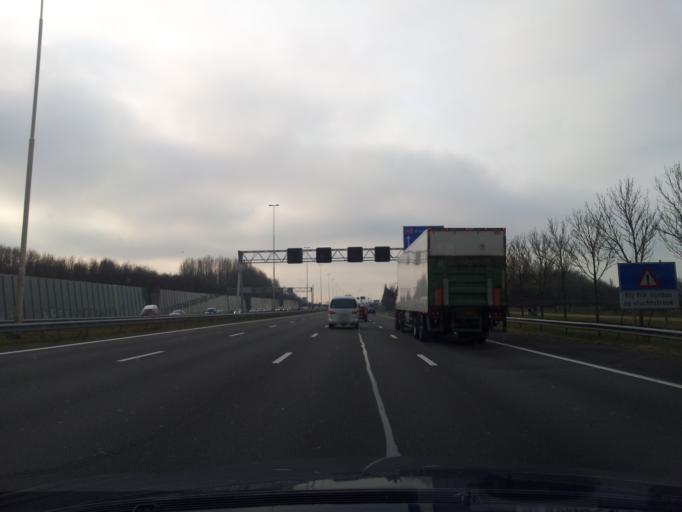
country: NL
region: Utrecht
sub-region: Gemeente Nieuwegein
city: Nieuwegein
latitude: 52.0118
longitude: 5.0705
